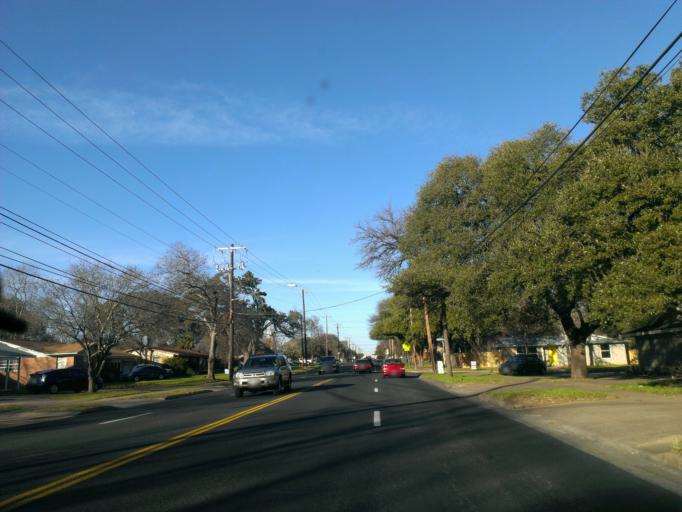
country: US
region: Texas
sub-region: Travis County
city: Rollingwood
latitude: 30.2246
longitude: -97.7917
